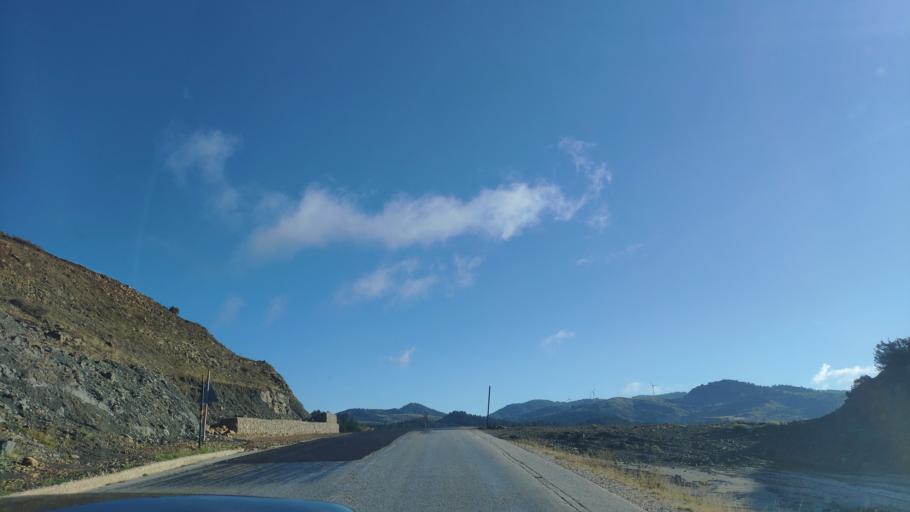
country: GR
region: Epirus
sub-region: Nomos Ioanninon
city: Metsovo
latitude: 39.7902
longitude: 21.1641
